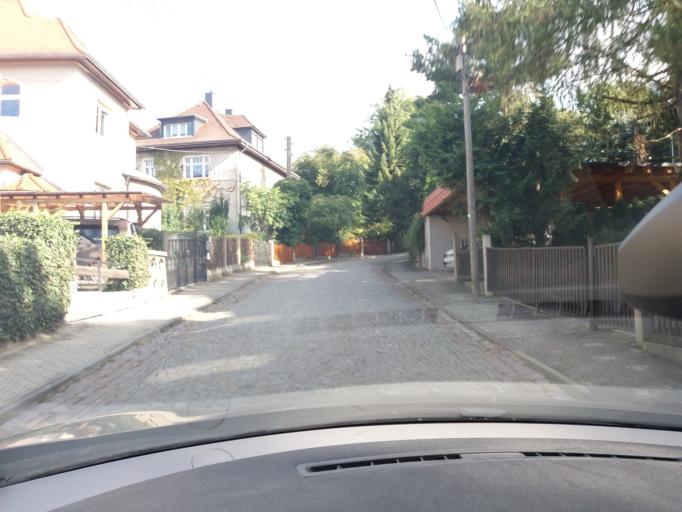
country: DE
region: Saxony
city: Radebeul
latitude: 51.0790
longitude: 13.6499
